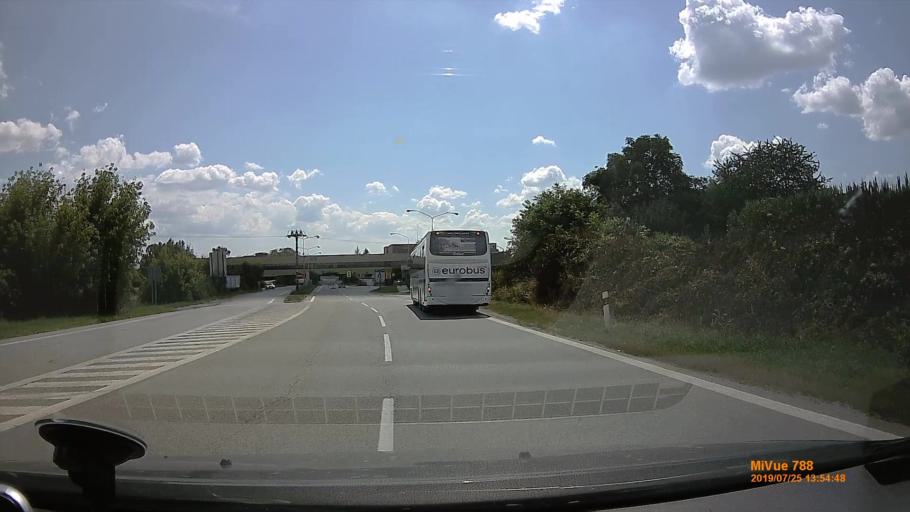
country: HU
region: Borsod-Abauj-Zemplen
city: Gonc
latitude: 48.5335
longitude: 21.2551
